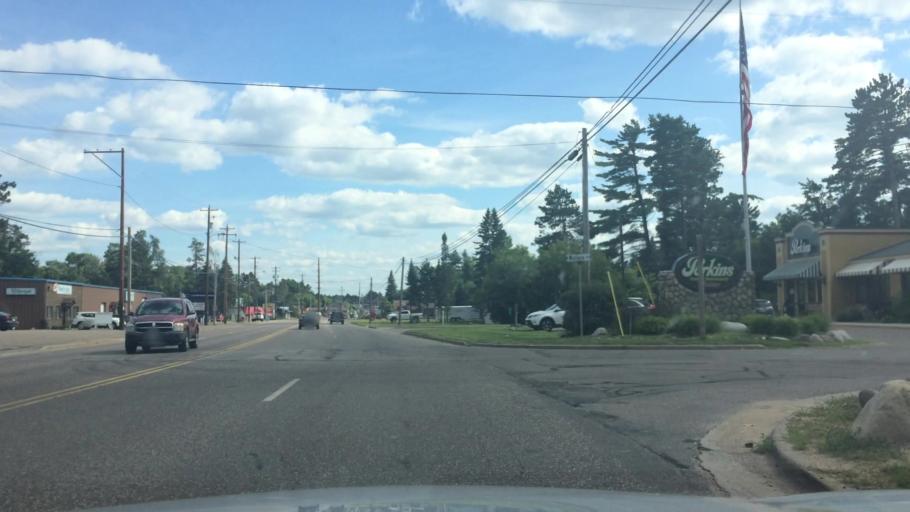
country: US
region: Wisconsin
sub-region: Vilas County
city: Lac du Flambeau
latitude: 45.9024
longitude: -89.6977
